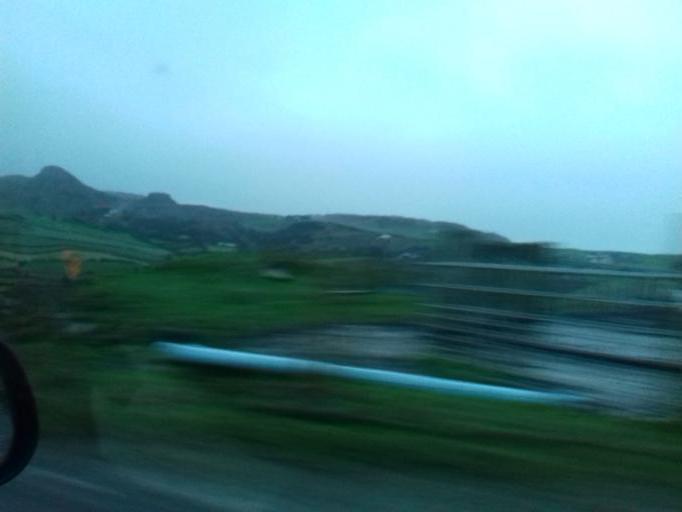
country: IE
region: Ulster
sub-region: County Donegal
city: Ramelton
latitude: 55.2458
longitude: -7.6725
